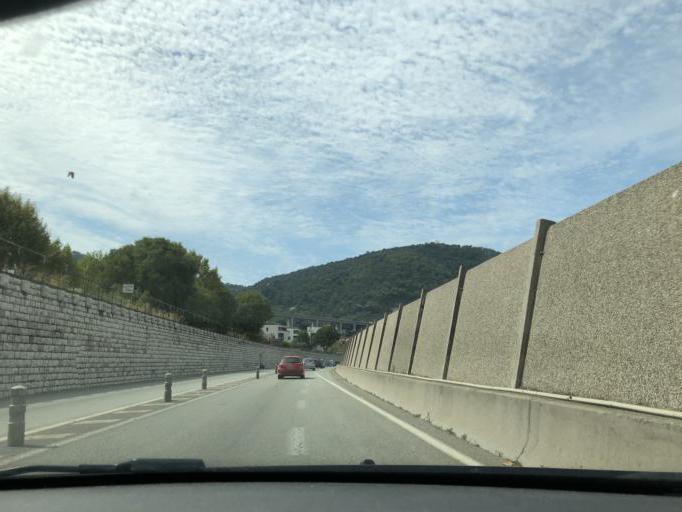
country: FR
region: Provence-Alpes-Cote d'Azur
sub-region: Departement des Alpes-Maritimes
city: La Trinite
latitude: 43.7394
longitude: 7.3097
